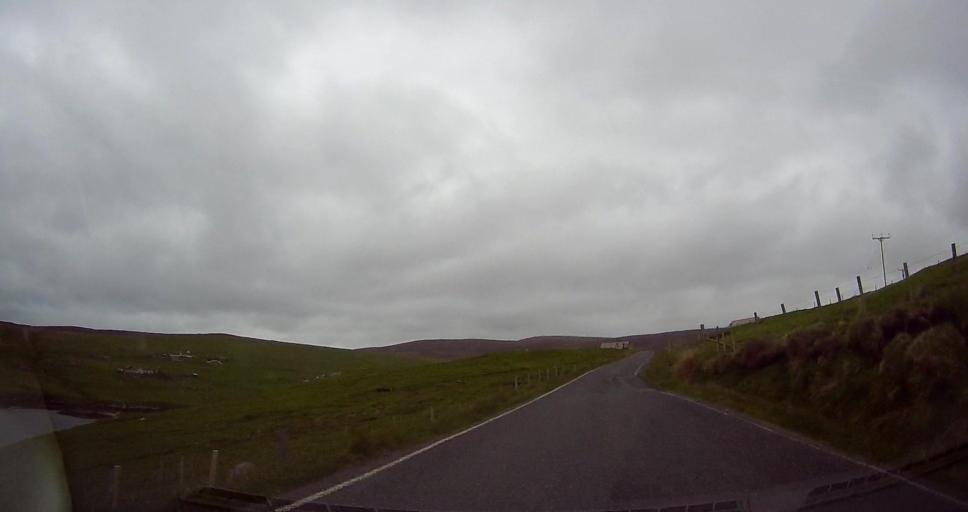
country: GB
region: Scotland
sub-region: Shetland Islands
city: Lerwick
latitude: 60.3010
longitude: -1.3548
